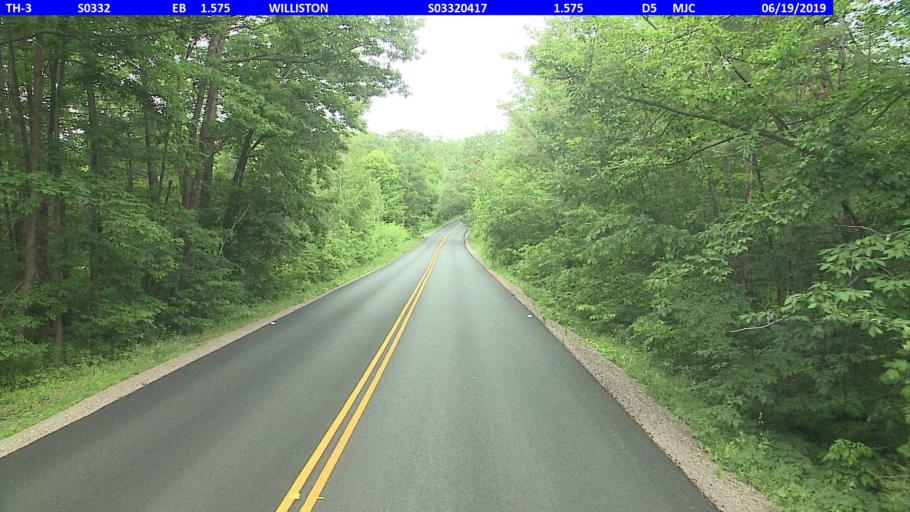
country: US
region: Vermont
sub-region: Chittenden County
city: Williston
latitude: 44.4197
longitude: -73.0934
